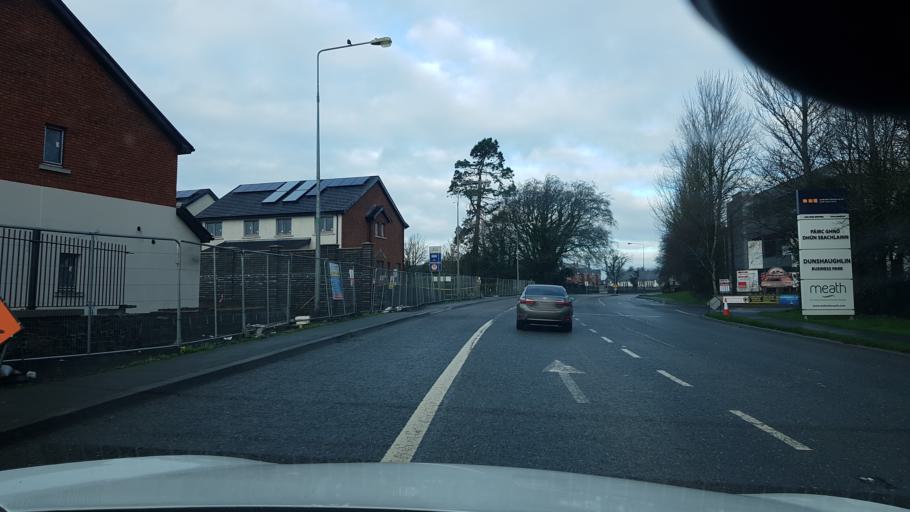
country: IE
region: Leinster
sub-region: An Mhi
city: Dunshaughlin
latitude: 53.5042
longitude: -6.5388
